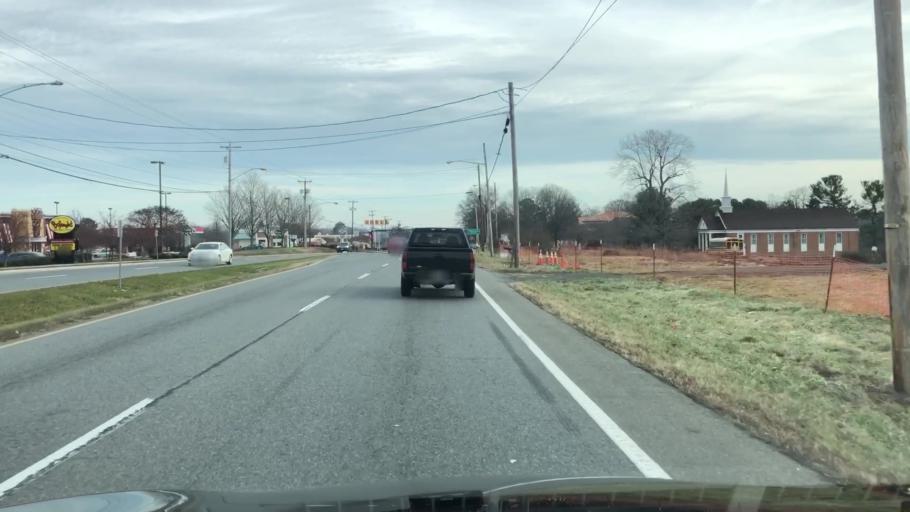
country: US
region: Virginia
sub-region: Campbell County
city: Timberlake
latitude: 37.3517
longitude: -79.2275
